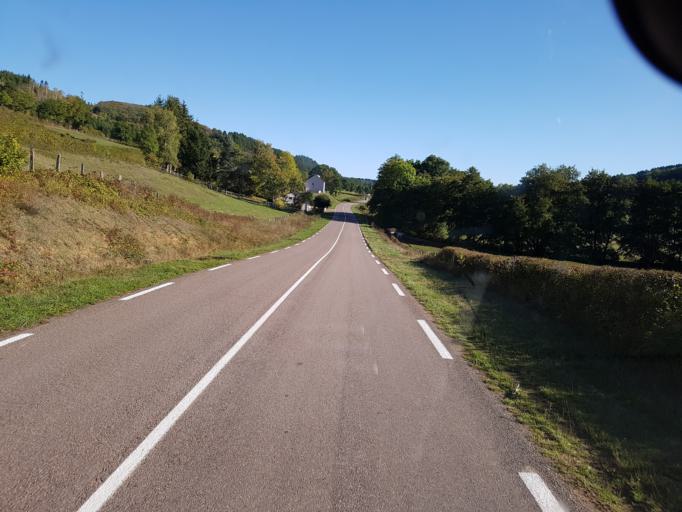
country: FR
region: Bourgogne
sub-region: Departement de Saone-et-Loire
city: Autun
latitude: 47.0969
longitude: 4.2328
